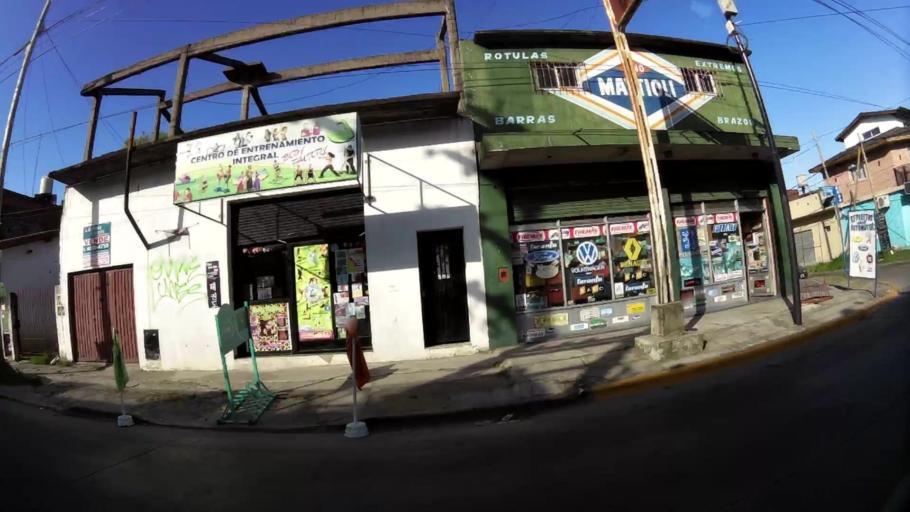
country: AR
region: Buenos Aires
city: Hurlingham
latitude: -34.5750
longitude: -58.6100
